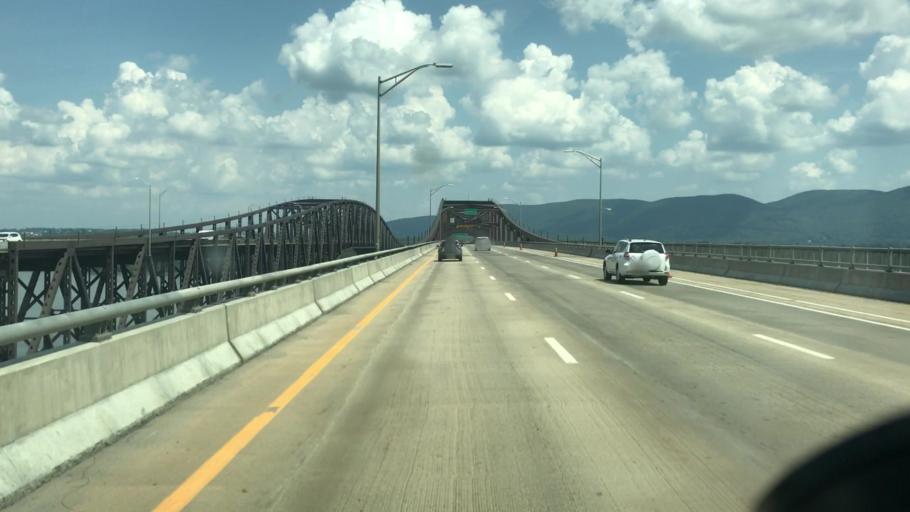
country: US
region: New York
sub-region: Orange County
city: Balmville
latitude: 41.5203
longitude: -74.0049
